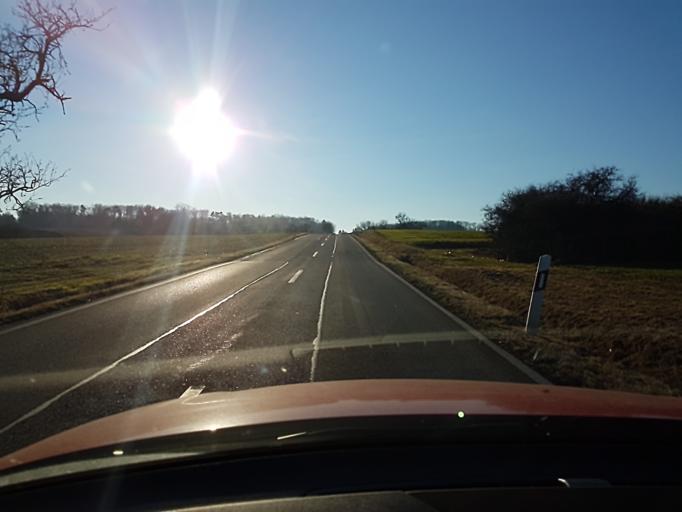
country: DE
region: Baden-Wuerttemberg
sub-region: Regierungsbezirk Stuttgart
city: Sersheim
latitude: 48.9945
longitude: 9.0134
